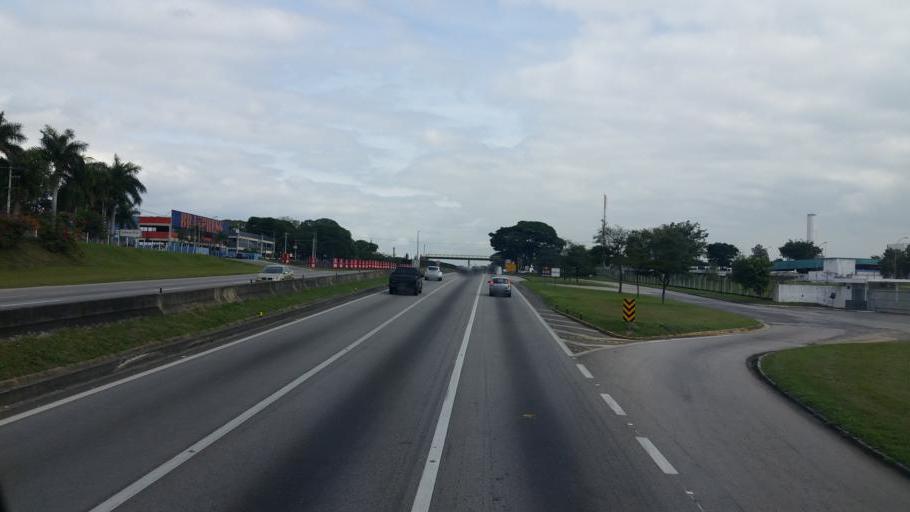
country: BR
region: Sao Paulo
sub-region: Jacarei
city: Jacarei
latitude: -23.2470
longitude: -45.9307
